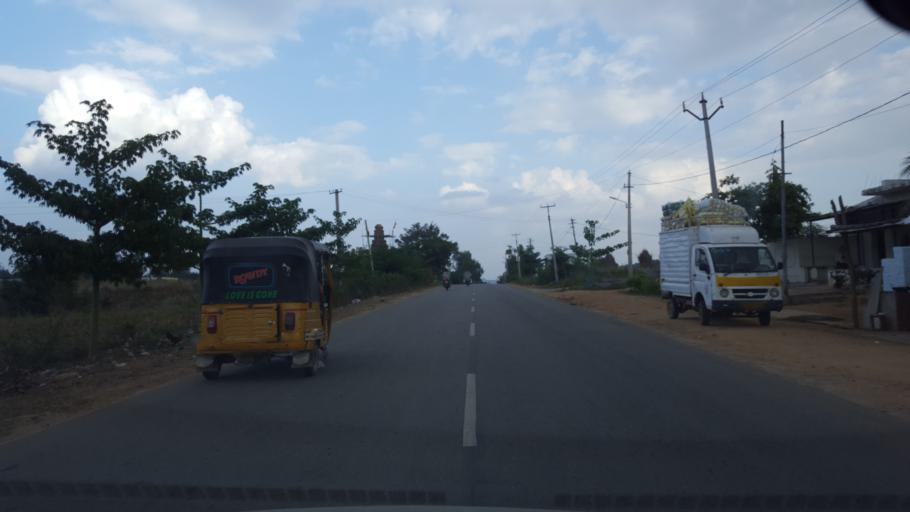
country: IN
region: Telangana
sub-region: Mahbubnagar
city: Mahbubnagar
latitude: 16.7600
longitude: 77.9575
